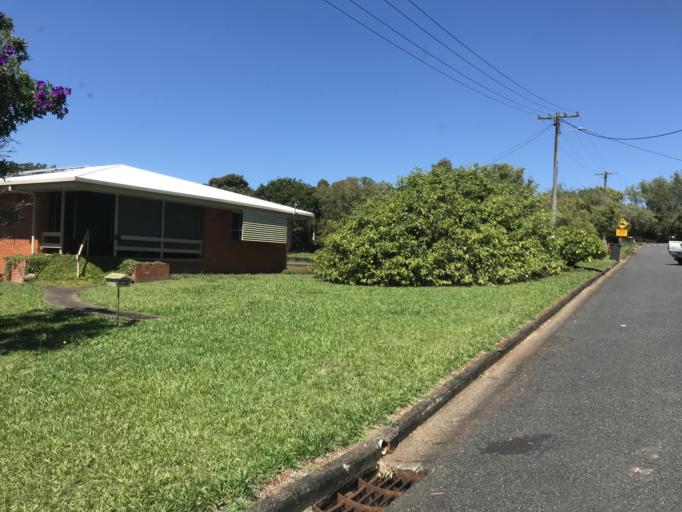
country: AU
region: Queensland
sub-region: Tablelands
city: Atherton
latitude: -17.3549
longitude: 145.5925
